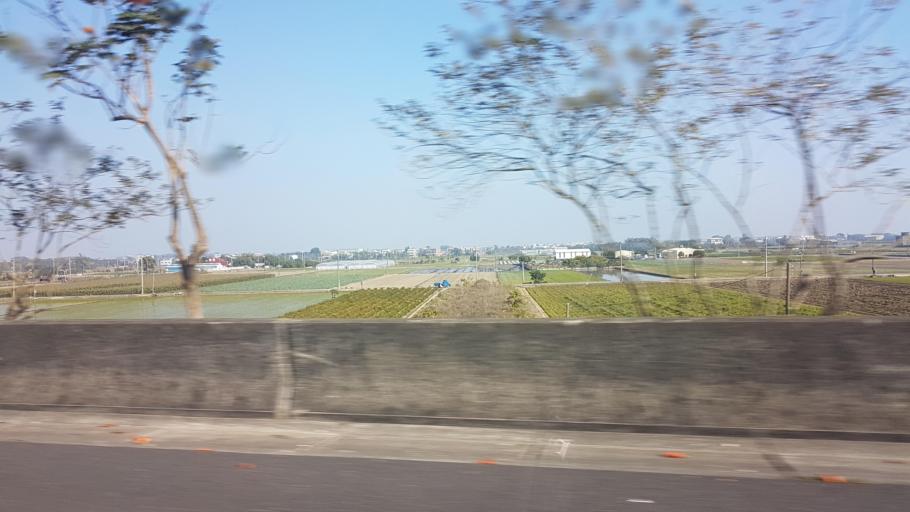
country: TW
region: Taiwan
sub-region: Chiayi
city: Taibao
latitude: 23.4207
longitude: 120.3748
